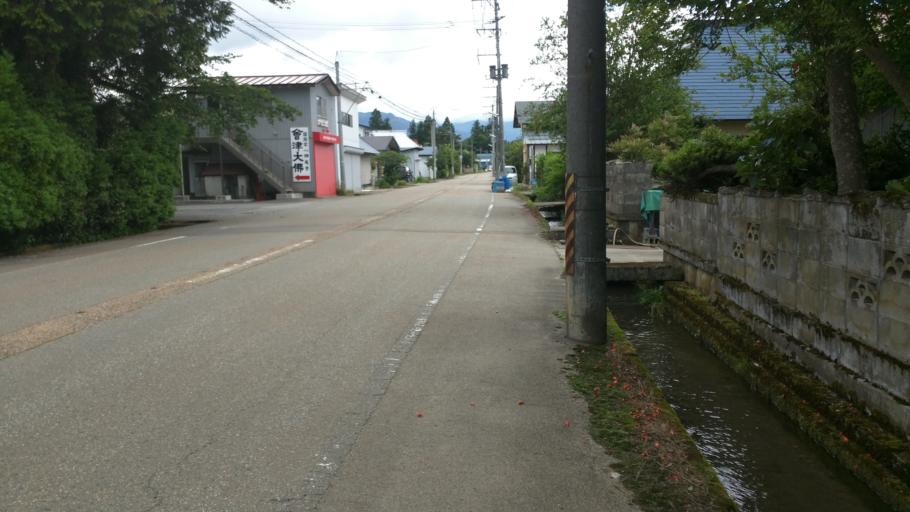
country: JP
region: Fukushima
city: Kitakata
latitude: 37.6874
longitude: 139.8644
